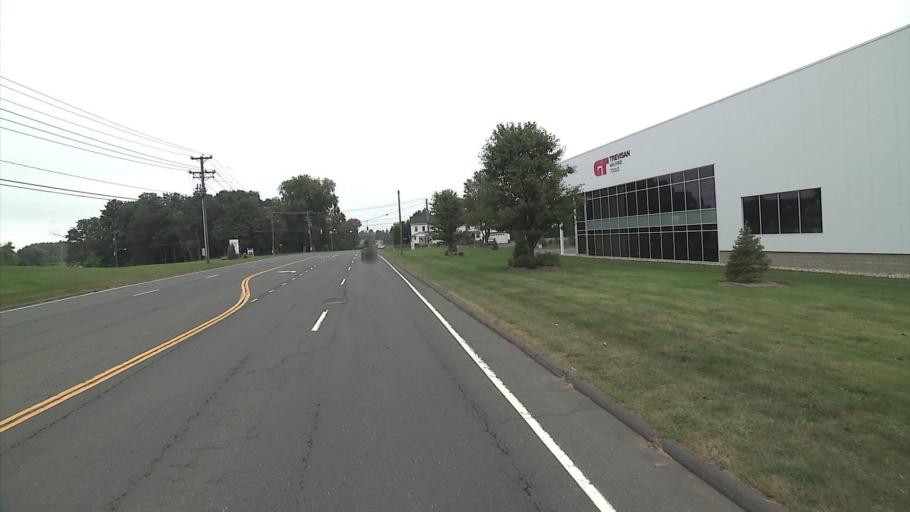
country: US
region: Connecticut
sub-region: Hartford County
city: Suffield Depot
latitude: 41.9614
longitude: -72.6626
